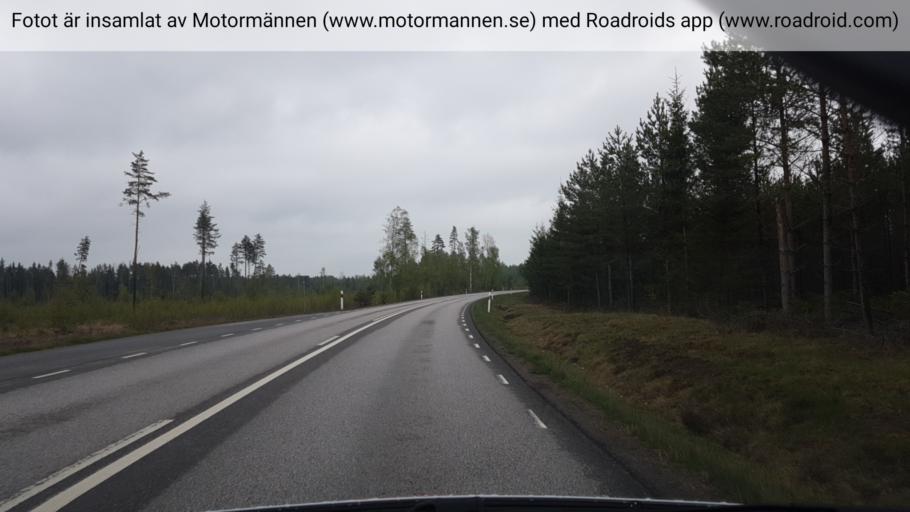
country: SE
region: Vaestra Goetaland
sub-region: Skovde Kommun
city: Stopen
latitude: 58.4434
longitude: 13.9371
